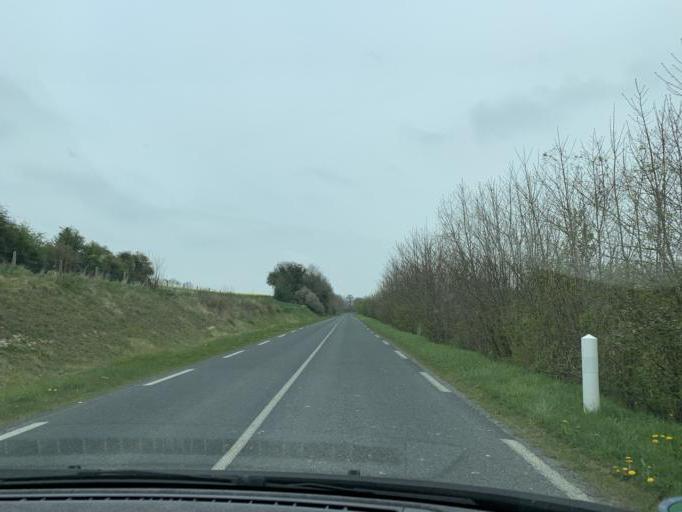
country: FR
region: Haute-Normandie
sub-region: Departement de la Seine-Maritime
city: Londinieres
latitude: 49.8428
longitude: 1.4640
